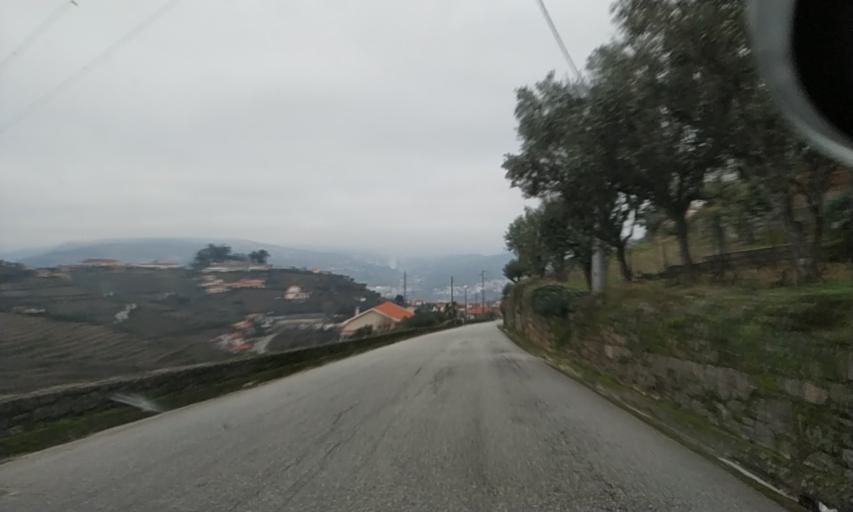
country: PT
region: Viseu
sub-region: Lamego
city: Lamego
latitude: 41.1198
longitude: -7.8037
